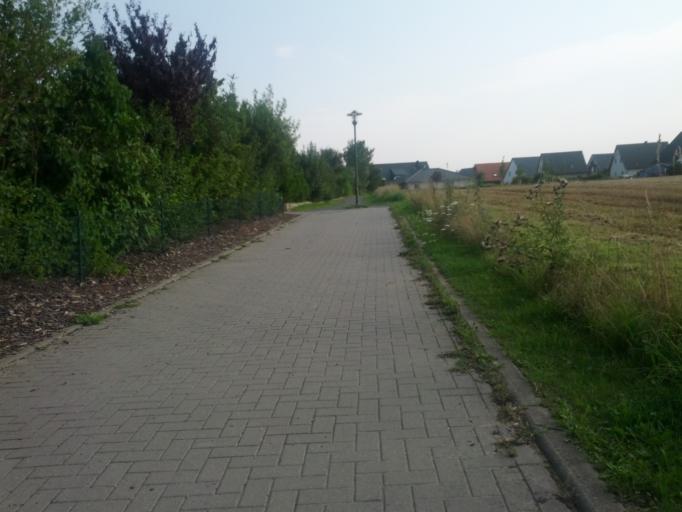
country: DE
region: Mecklenburg-Vorpommern
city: Ostseebad Kuhlungsborn
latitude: 54.1448
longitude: 11.7309
